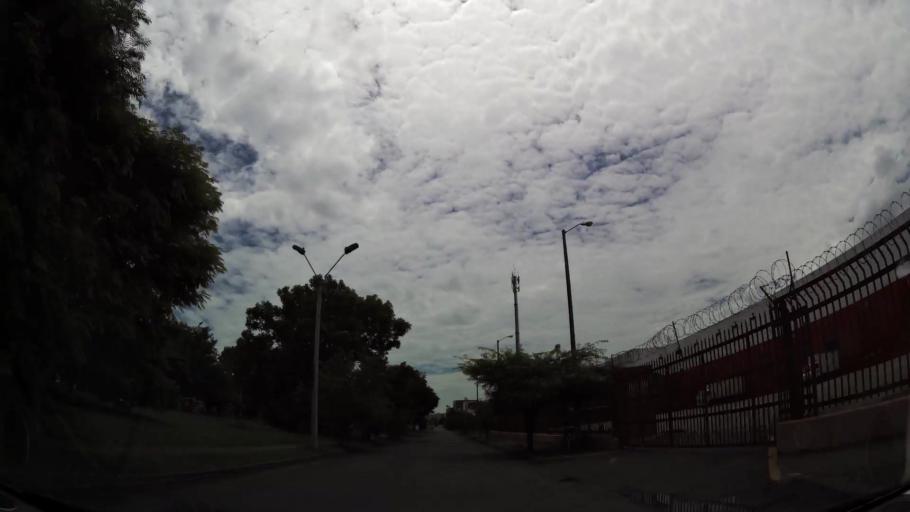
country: CO
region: Valle del Cauca
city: Cali
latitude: 3.3742
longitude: -76.5226
